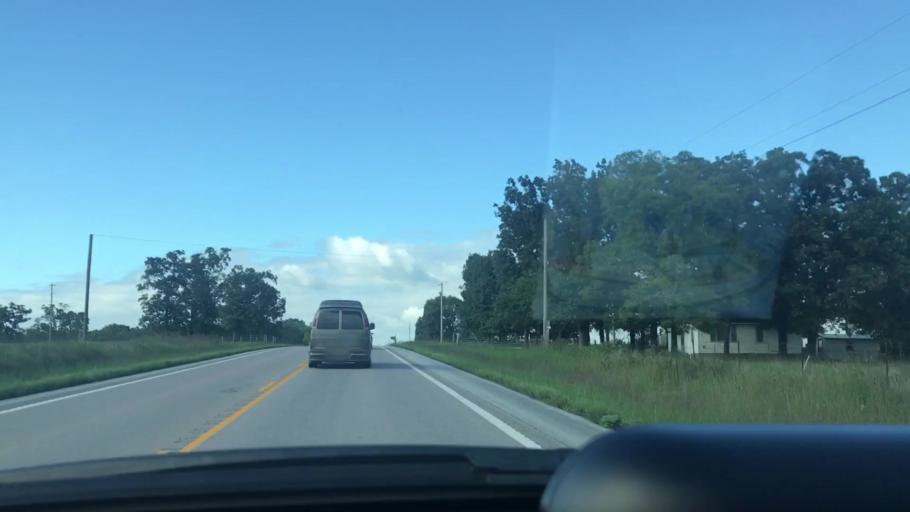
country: US
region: Missouri
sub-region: Hickory County
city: Hermitage
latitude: 37.9727
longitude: -93.2063
